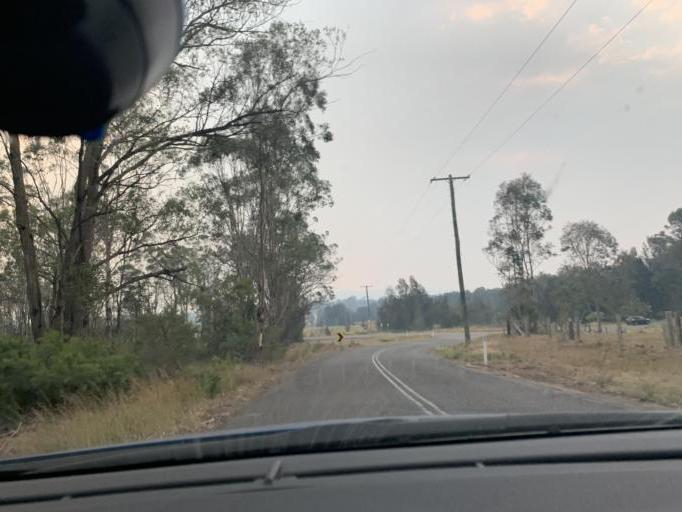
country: AU
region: New South Wales
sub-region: Cessnock
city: Cessnock
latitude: -32.9277
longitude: 151.3153
